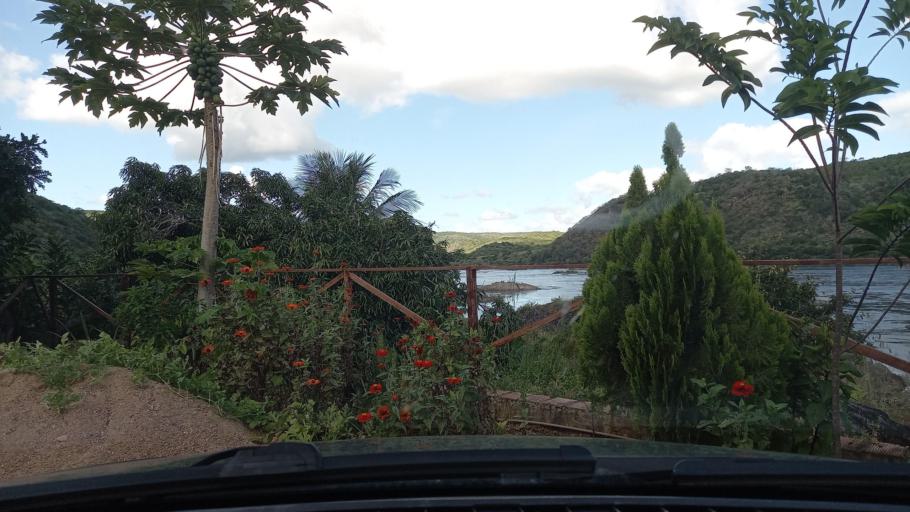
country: BR
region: Sergipe
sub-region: Caninde De Sao Francisco
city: Caninde de Sao Francisco
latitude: -9.6237
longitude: -37.7492
